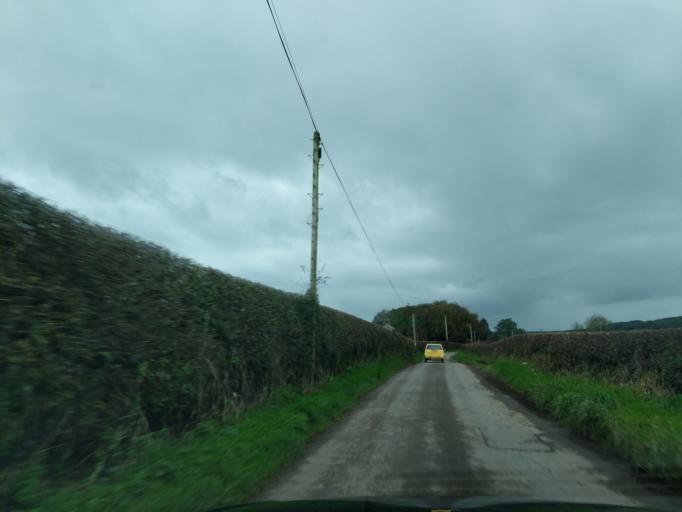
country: GB
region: Scotland
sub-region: Dumfries and Galloway
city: Kirkcudbright
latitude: 54.8904
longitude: -3.9966
